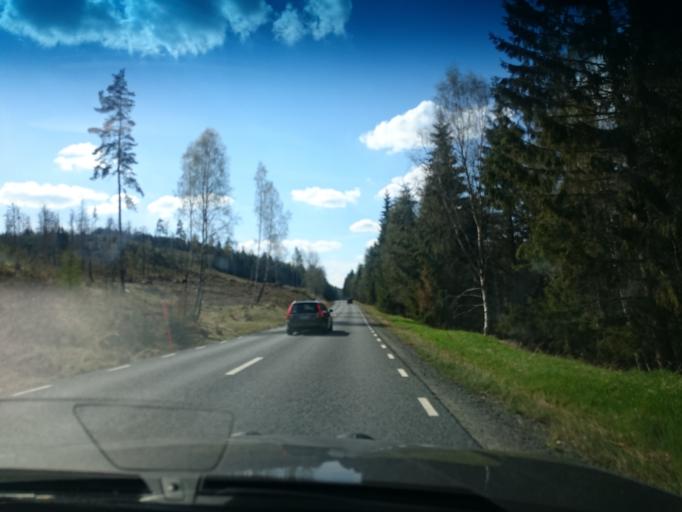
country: SE
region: Joenkoeping
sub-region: Vetlanda Kommun
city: Vetlanda
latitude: 57.3654
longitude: 15.2515
